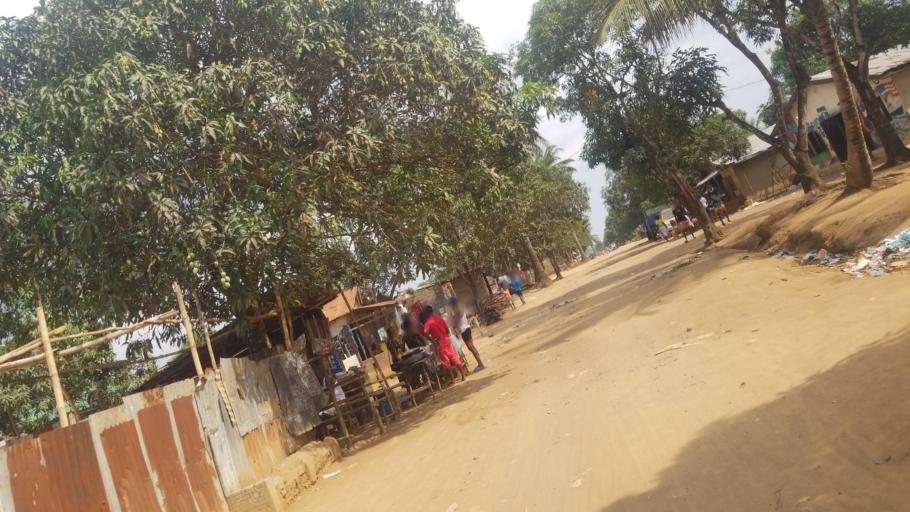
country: SL
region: Western Area
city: Waterloo
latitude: 8.3408
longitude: -13.0528
